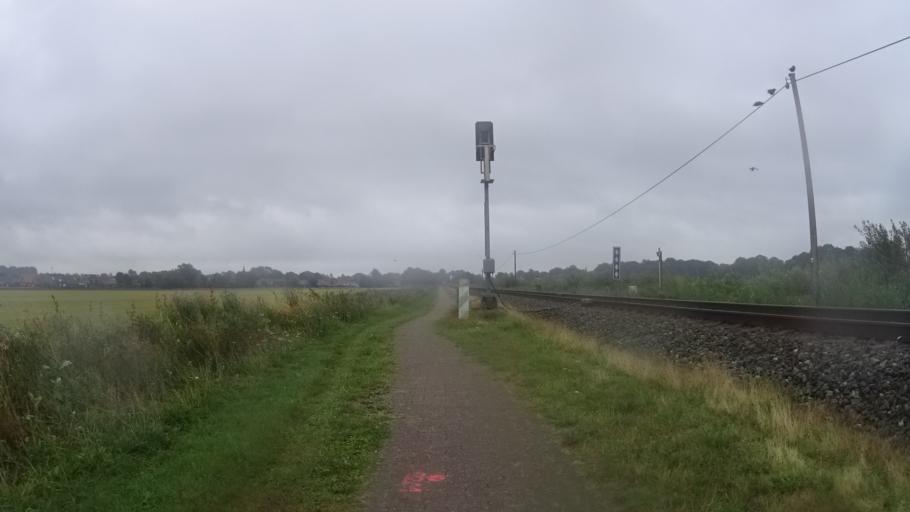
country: DE
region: Lower Saxony
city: Bunde
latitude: 53.1869
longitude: 7.2536
